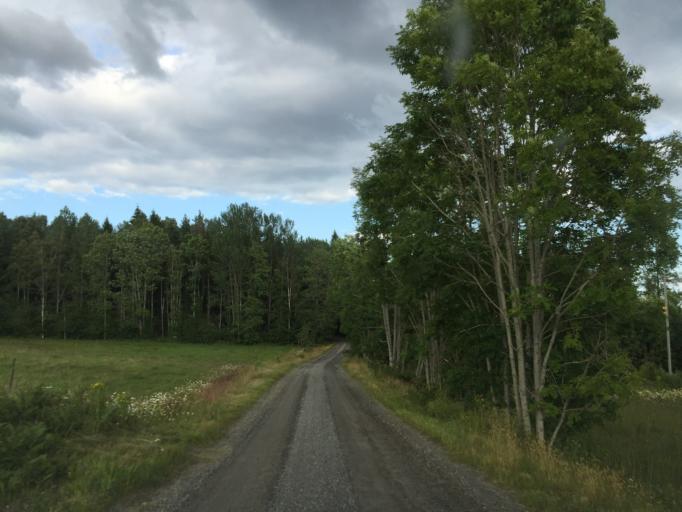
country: SE
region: OEstergoetland
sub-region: Motala Kommun
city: Ryd
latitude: 58.7132
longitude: 15.0285
